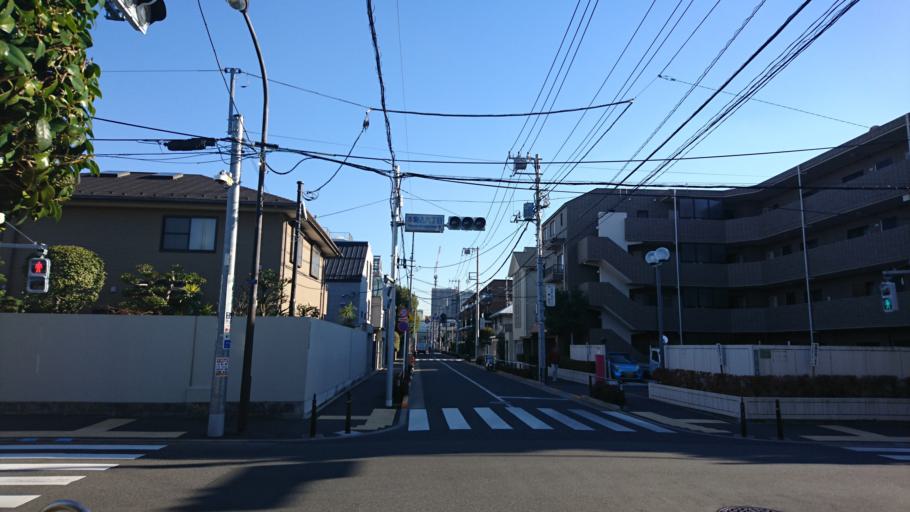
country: JP
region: Tokyo
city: Tokyo
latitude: 35.7322
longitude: 139.7425
